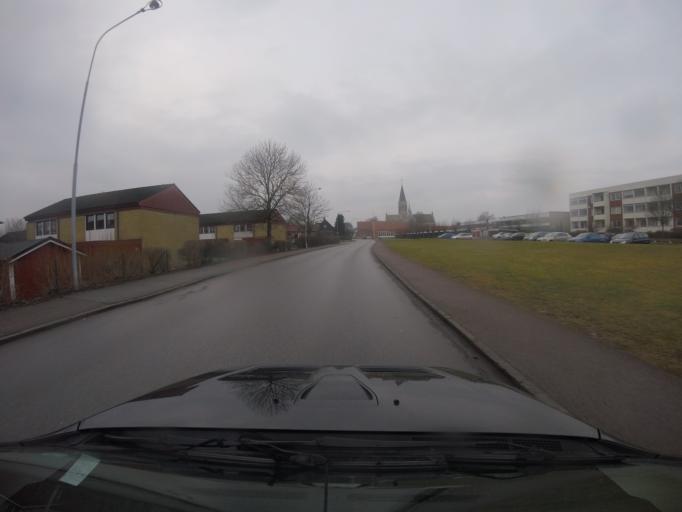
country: SE
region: Skane
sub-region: Svedala Kommun
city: Svedala
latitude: 55.5117
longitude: 13.2291
